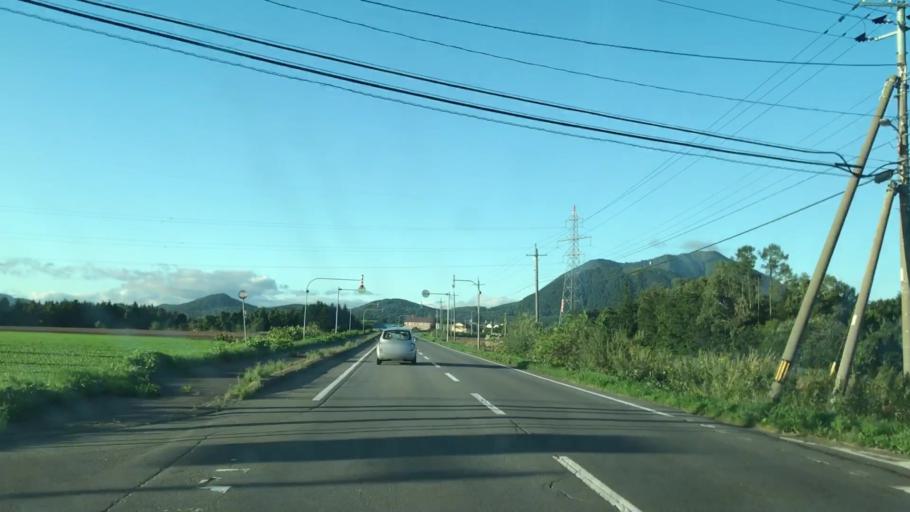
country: JP
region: Hokkaido
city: Niseko Town
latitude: 42.7192
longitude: 140.8600
